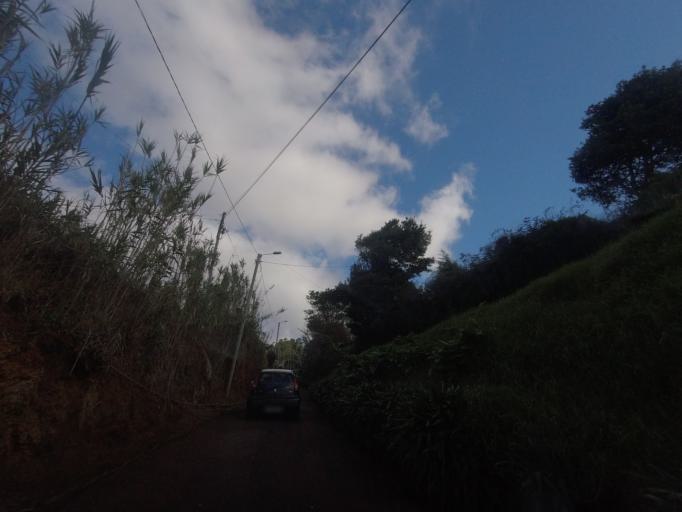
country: PT
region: Madeira
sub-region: Calheta
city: Faja da Ovelha
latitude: 32.8266
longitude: -17.2336
